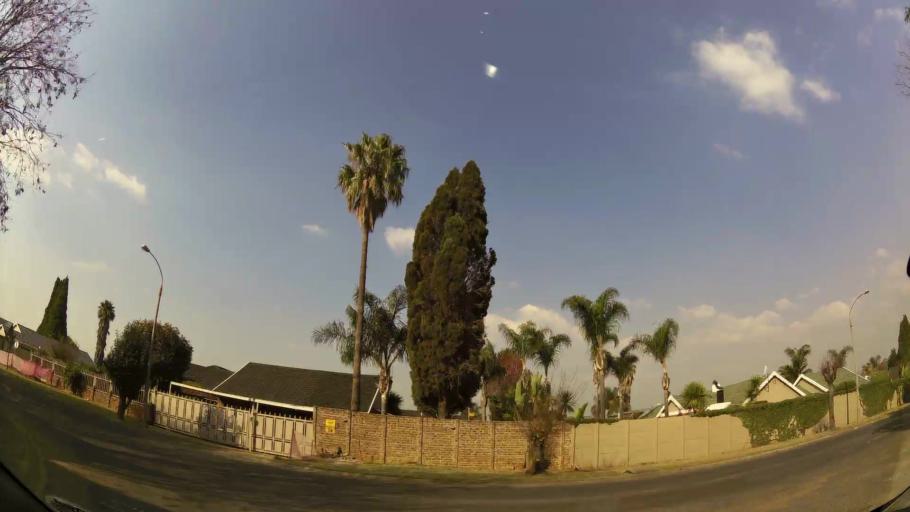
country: ZA
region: Gauteng
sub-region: Ekurhuleni Metropolitan Municipality
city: Benoni
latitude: -26.1608
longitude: 28.2804
